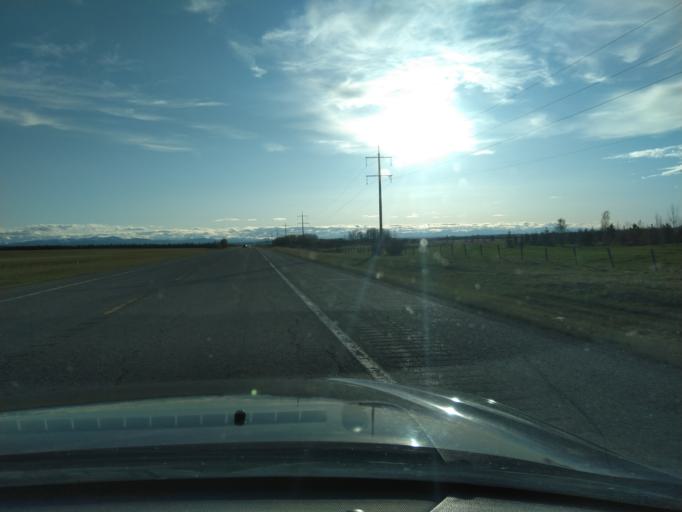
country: CA
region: Alberta
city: Cochrane
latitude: 51.0234
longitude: -114.3513
